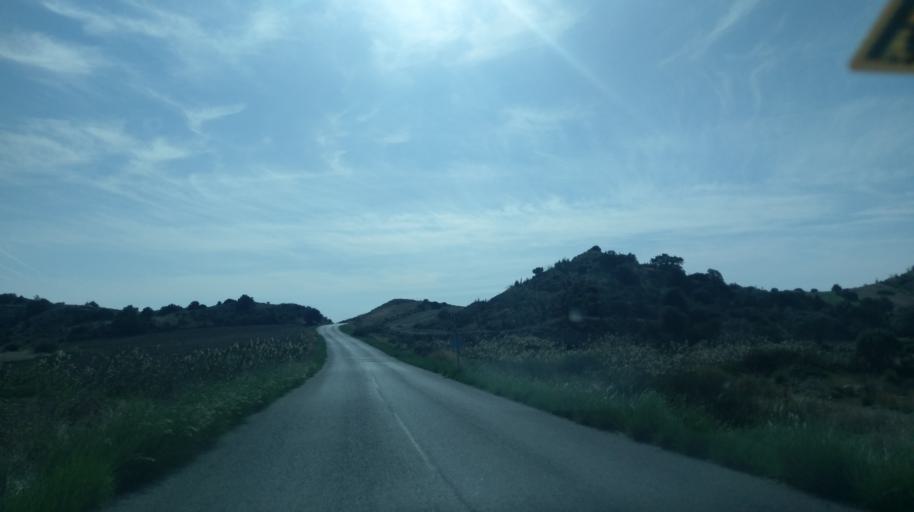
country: CY
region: Ammochostos
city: Trikomo
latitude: 35.3464
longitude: 33.9306
